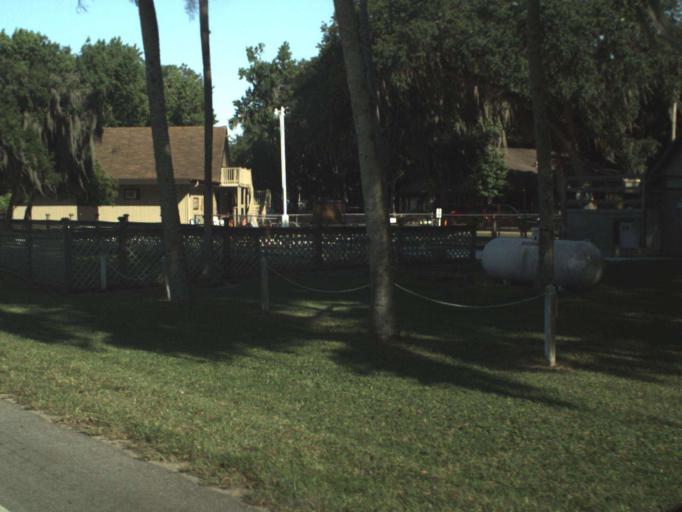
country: US
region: Florida
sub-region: Brevard County
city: Mims
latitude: 28.6661
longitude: -80.8759
